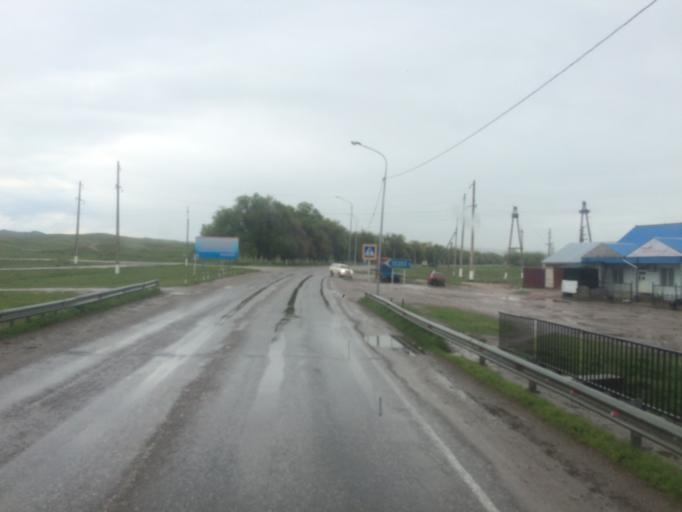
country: KZ
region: Zhambyl
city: Georgiyevka
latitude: 43.2361
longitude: 74.7596
